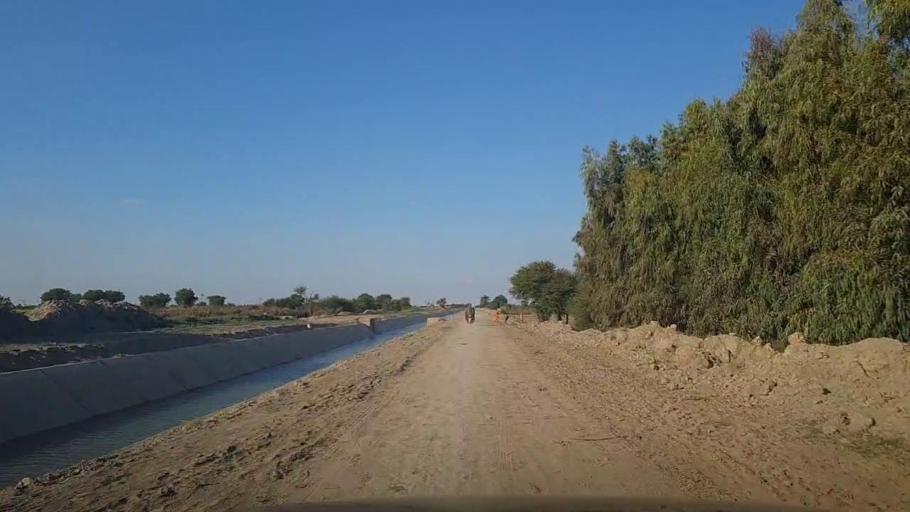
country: PK
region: Sindh
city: Jhol
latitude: 25.8999
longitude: 69.0391
